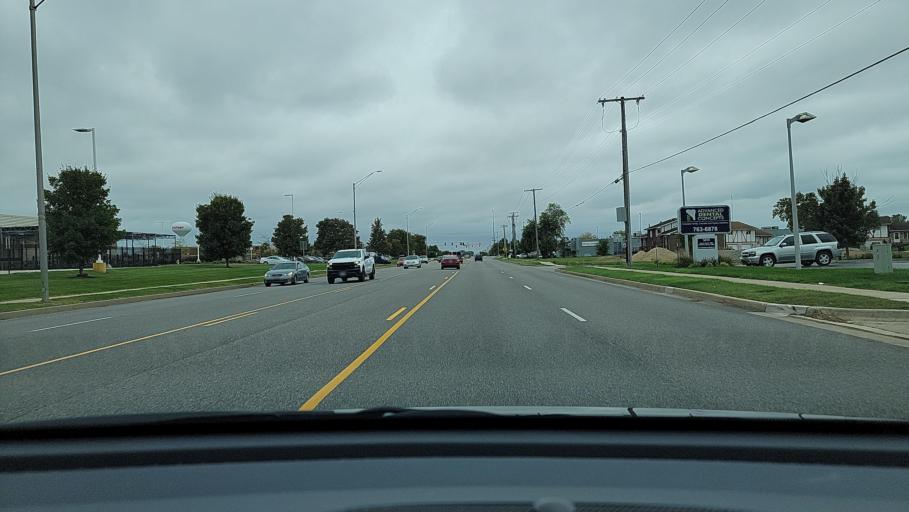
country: US
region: Indiana
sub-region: Porter County
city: Portage
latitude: 41.5534
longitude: -87.1827
